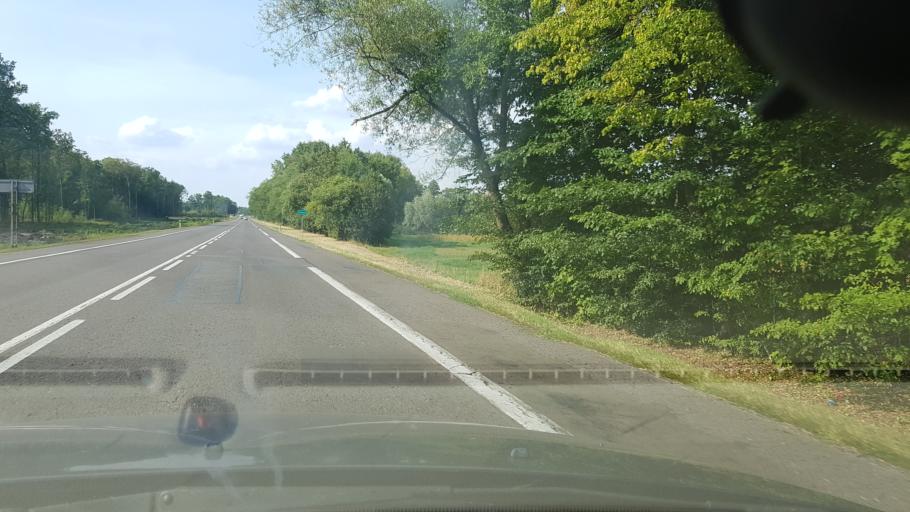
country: PL
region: Masovian Voivodeship
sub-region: Powiat ciechanowski
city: Glinojeck
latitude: 52.7446
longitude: 20.3167
